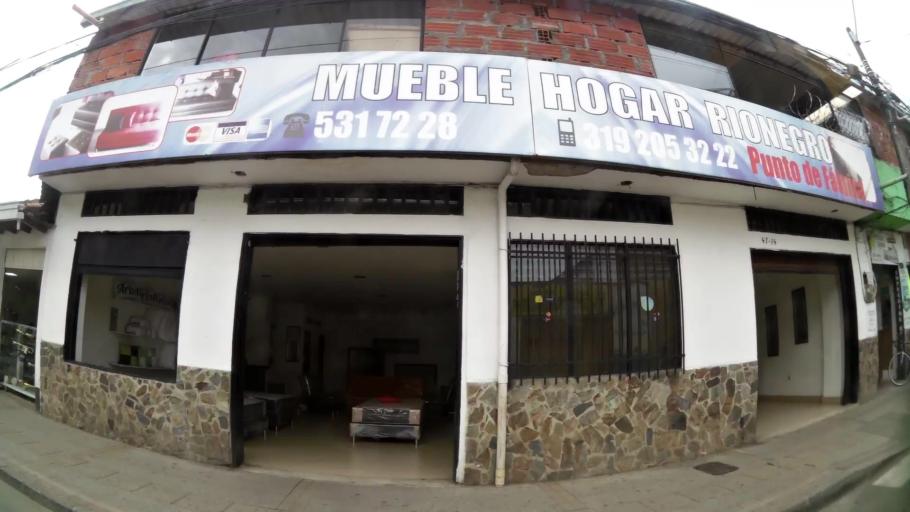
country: CO
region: Antioquia
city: Rionegro
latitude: 6.1541
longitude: -75.3703
